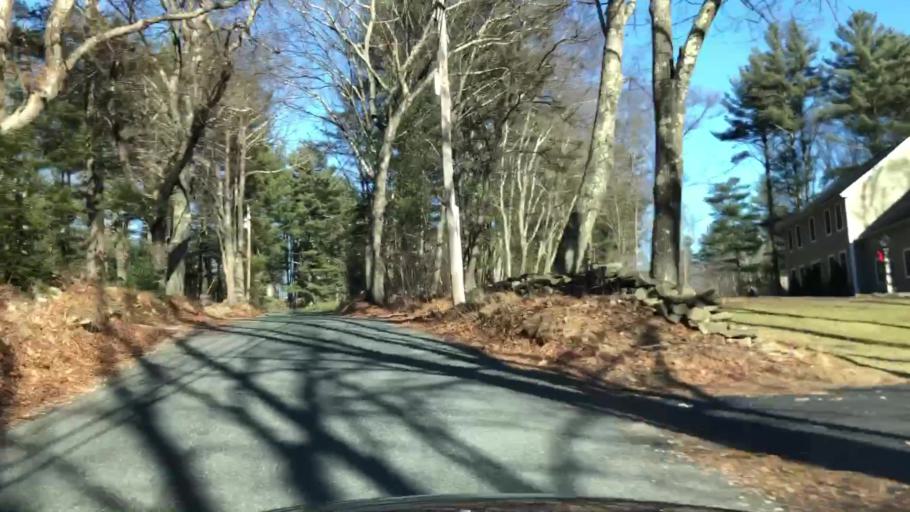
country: US
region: Massachusetts
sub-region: Worcester County
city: Charlton
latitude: 42.1014
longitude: -71.9770
